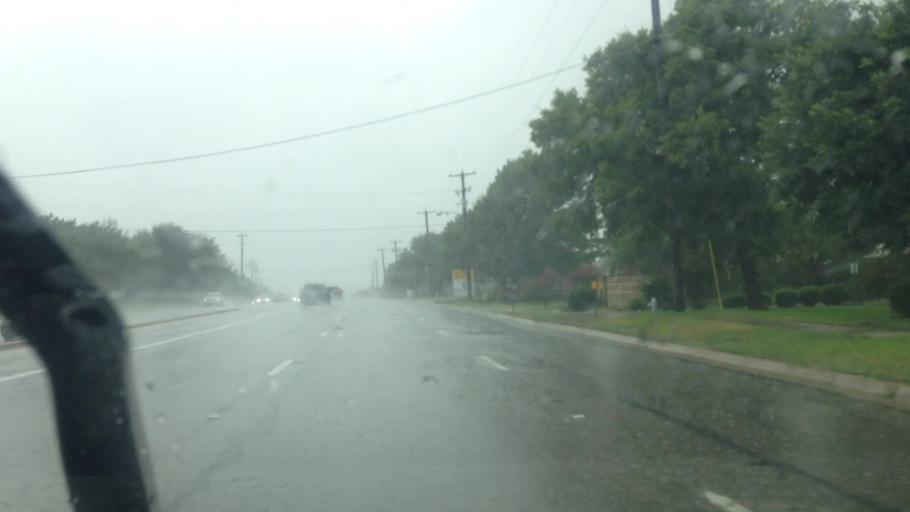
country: US
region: Texas
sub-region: Tarrant County
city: Keller
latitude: 32.9345
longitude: -97.2457
